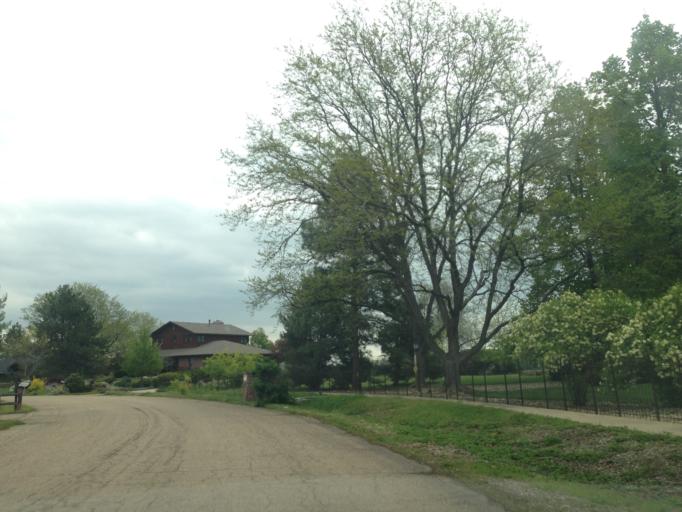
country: US
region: Colorado
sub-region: Boulder County
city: Louisville
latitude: 40.0051
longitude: -105.1701
